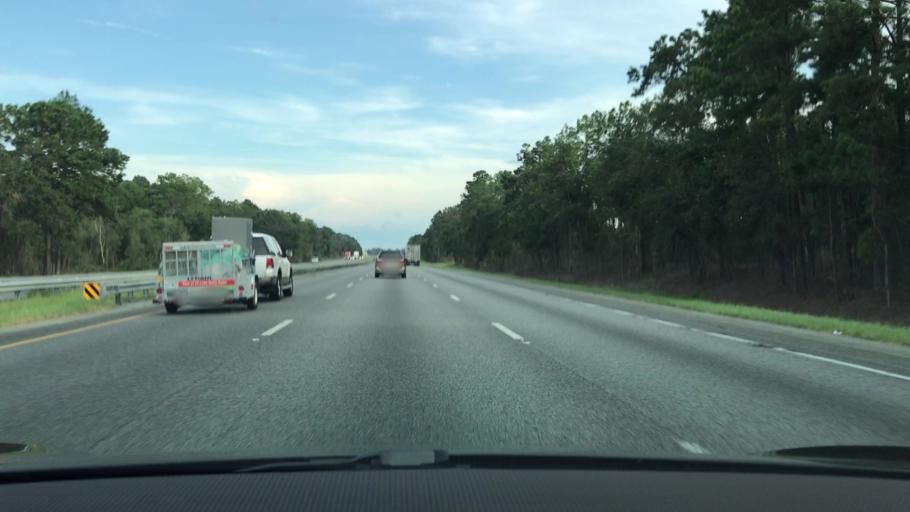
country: US
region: Georgia
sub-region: Lowndes County
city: Valdosta
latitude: 30.7161
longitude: -83.2539
